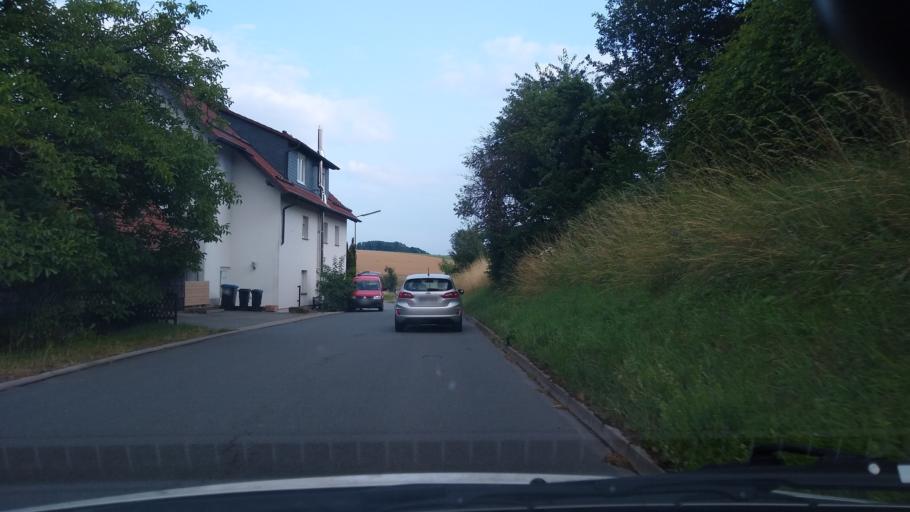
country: DE
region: Hesse
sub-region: Regierungsbezirk Darmstadt
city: Erbach
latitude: 49.6867
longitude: 8.9205
